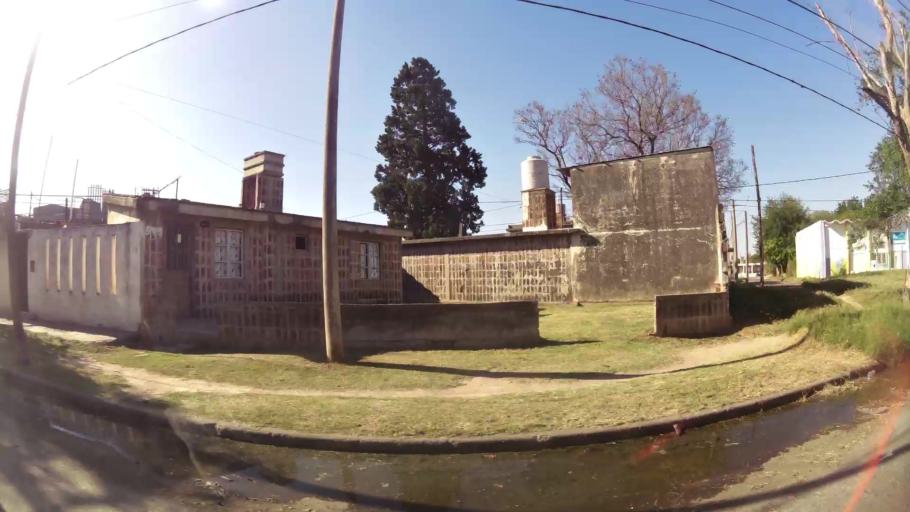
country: AR
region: Cordoba
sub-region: Departamento de Capital
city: Cordoba
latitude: -31.3873
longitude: -64.1646
